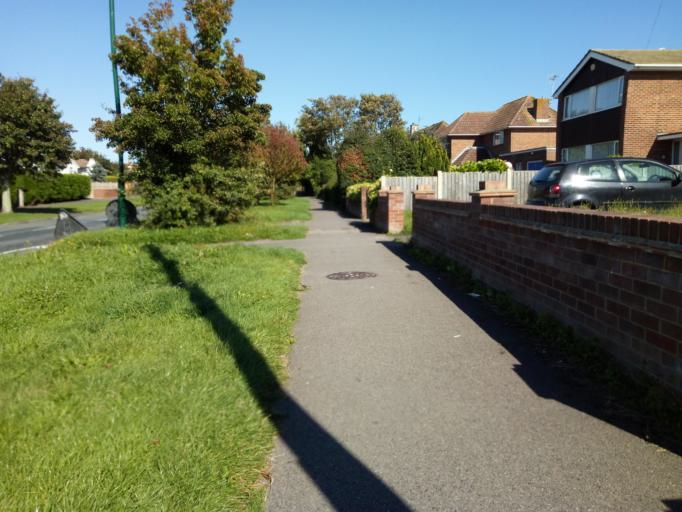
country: GB
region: England
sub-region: West Sussex
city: Barnham
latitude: 50.7941
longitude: -0.6365
